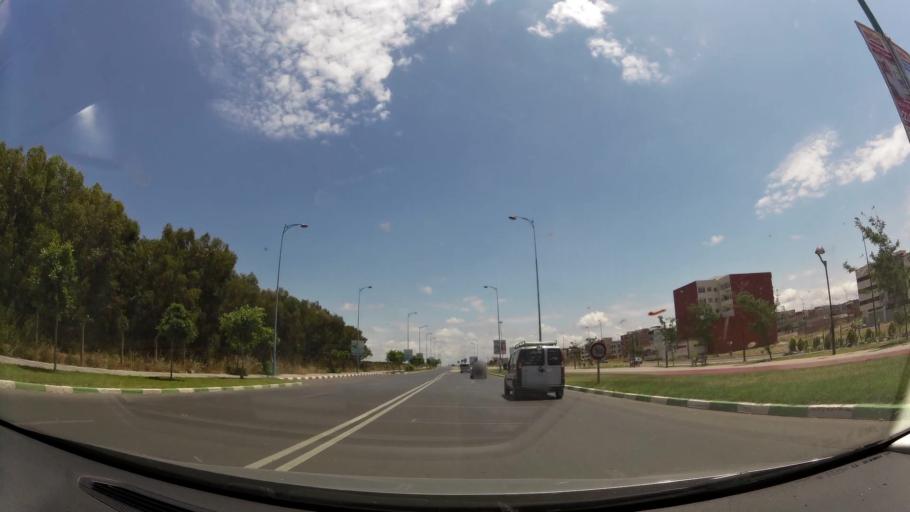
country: MA
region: Gharb-Chrarda-Beni Hssen
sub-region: Kenitra Province
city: Kenitra
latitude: 34.2729
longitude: -6.6230
